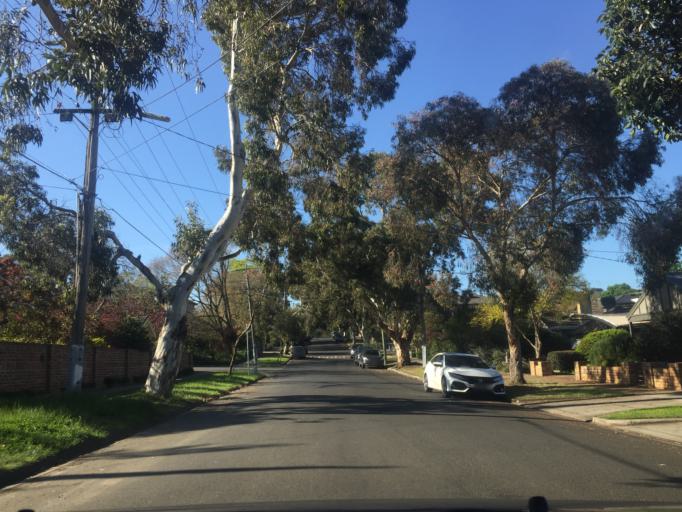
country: AU
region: Victoria
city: Ivanhoe East
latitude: -37.7765
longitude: 145.0594
